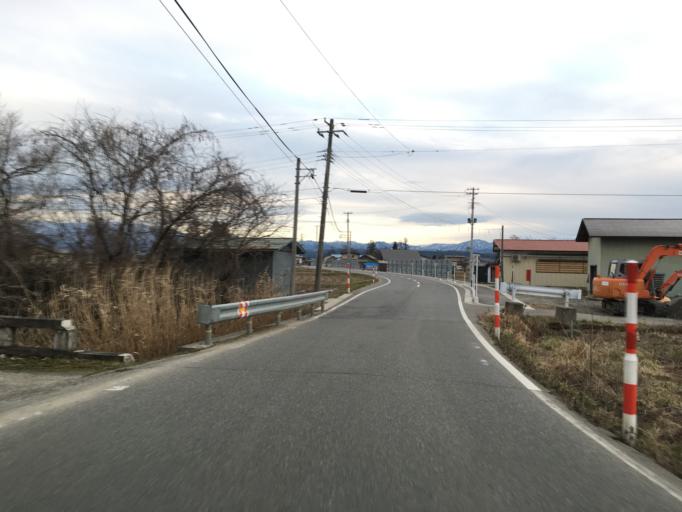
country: JP
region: Yamagata
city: Nagai
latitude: 38.0074
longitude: 140.0763
